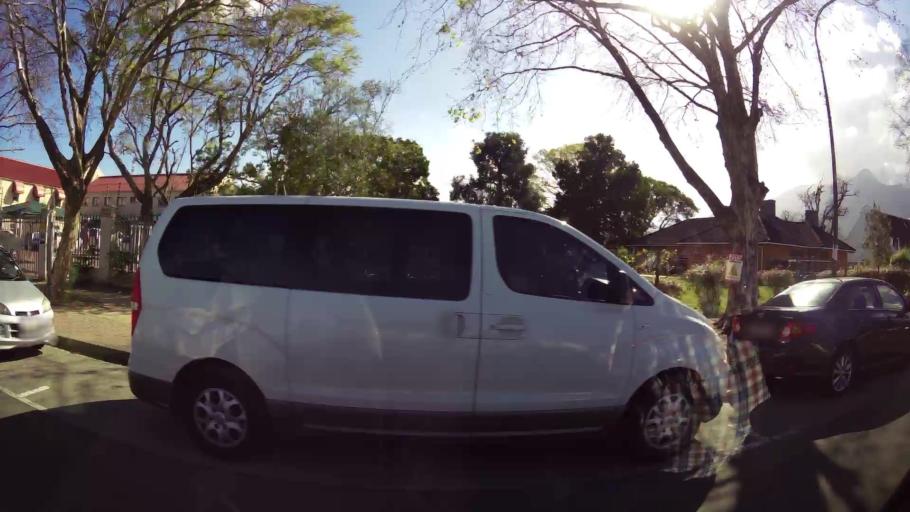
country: ZA
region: Western Cape
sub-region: Eden District Municipality
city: George
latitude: -33.9591
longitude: 22.4607
